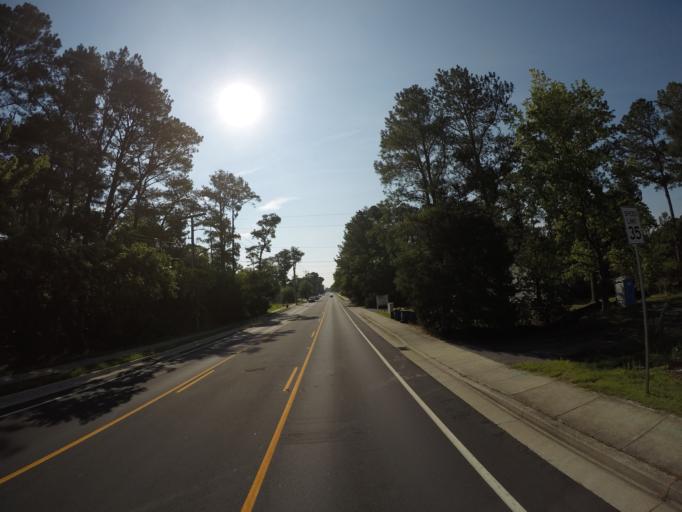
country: US
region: Delaware
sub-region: Sussex County
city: Ocean View
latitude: 38.5422
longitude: -75.0793
